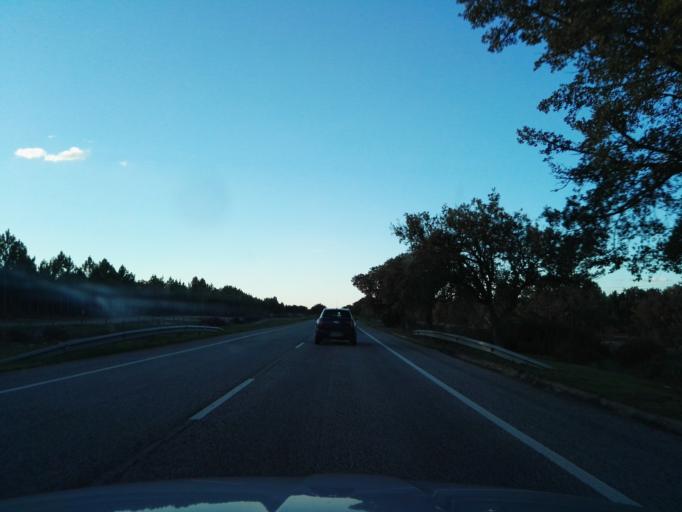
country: PT
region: Santarem
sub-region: Benavente
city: Poceirao
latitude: 38.8798
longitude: -8.8134
